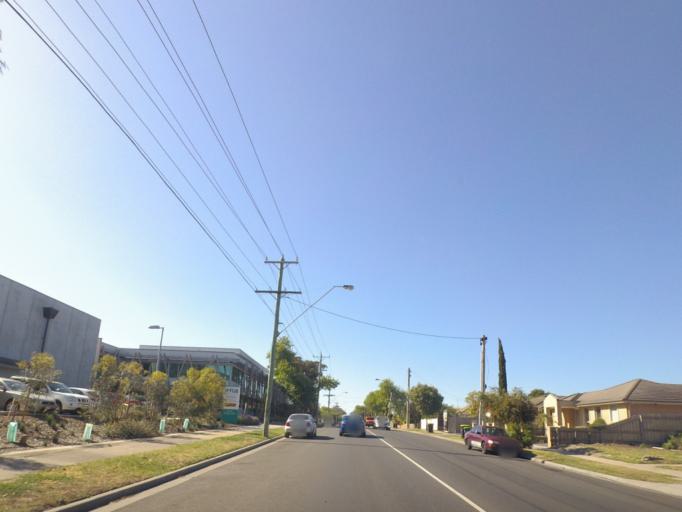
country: AU
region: Victoria
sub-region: Monash
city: Oakleigh South
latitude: -37.9331
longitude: 145.0994
